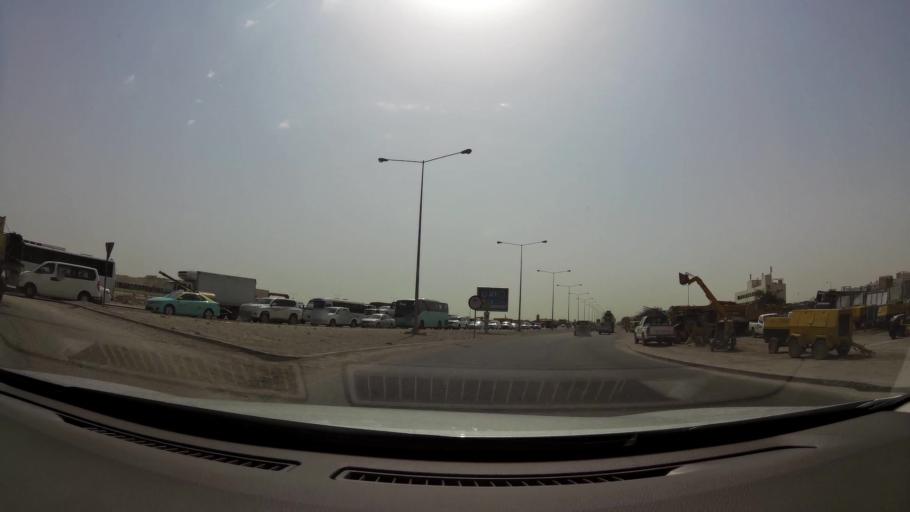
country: QA
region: Al Wakrah
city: Al Wukayr
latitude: 25.1844
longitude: 51.4607
